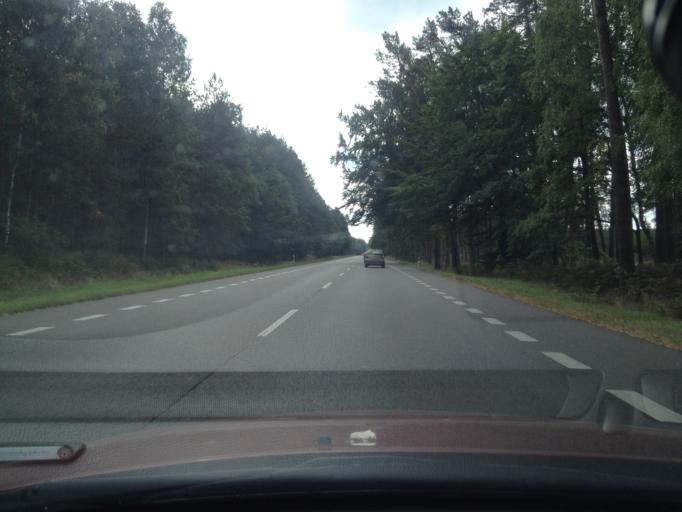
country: PL
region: West Pomeranian Voivodeship
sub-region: Powiat goleniowski
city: Przybiernow
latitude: 53.6984
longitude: 14.7880
